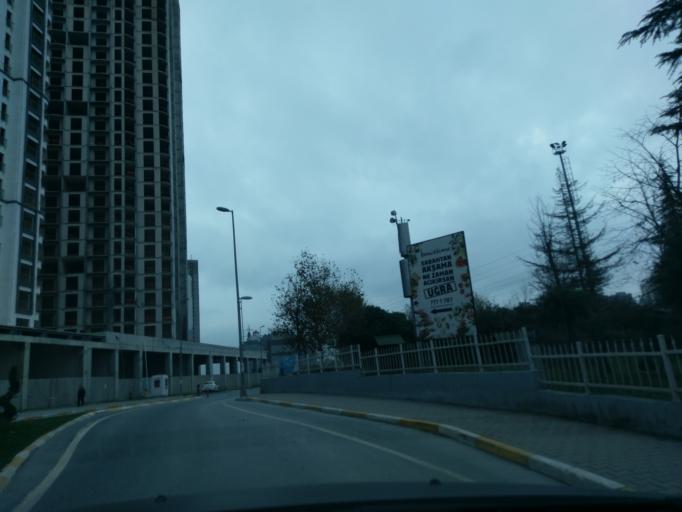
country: TR
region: Istanbul
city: Esenyurt
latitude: 41.0190
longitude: 28.6720
